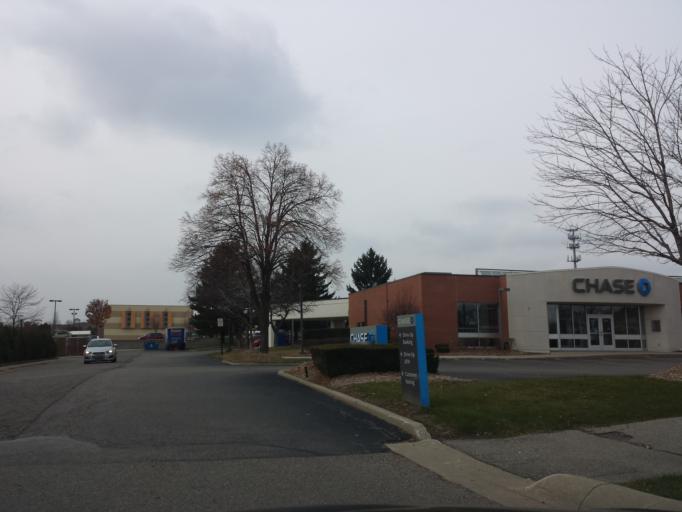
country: US
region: Michigan
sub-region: Oakland County
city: Auburn Hills
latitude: 42.6817
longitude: -83.1943
